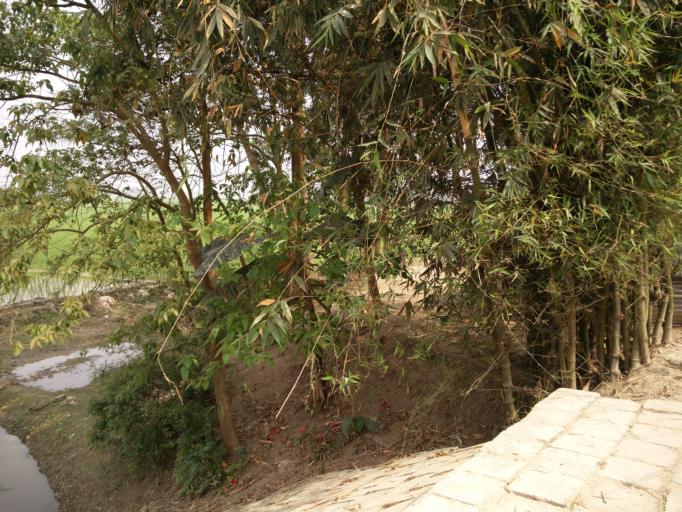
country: BD
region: Rangpur Division
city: Nageswari
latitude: 25.8869
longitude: 89.7344
